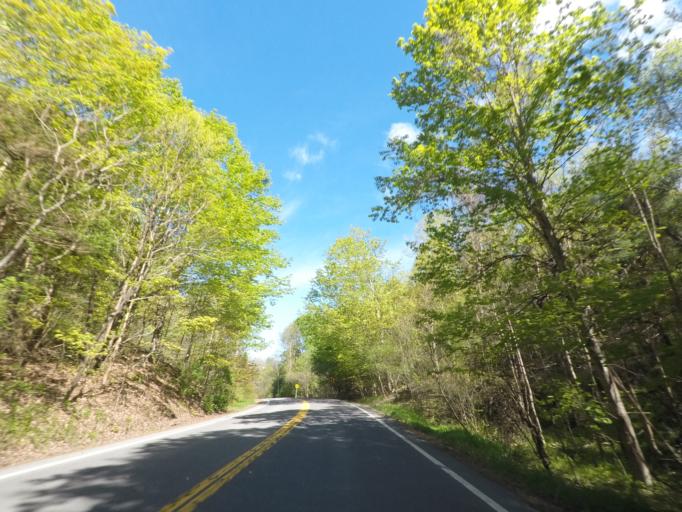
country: US
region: New York
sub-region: Albany County
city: Ravena
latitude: 42.4816
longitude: -73.9260
